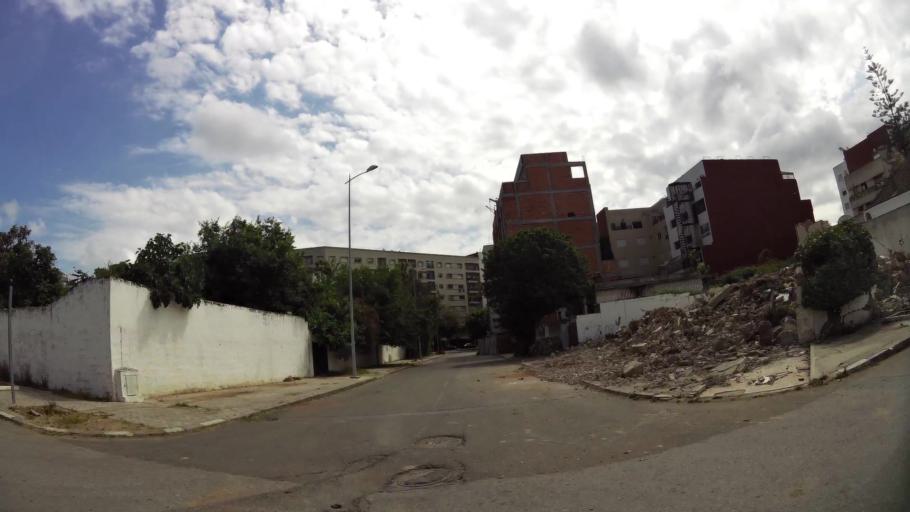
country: MA
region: Gharb-Chrarda-Beni Hssen
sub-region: Kenitra Province
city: Kenitra
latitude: 34.2558
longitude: -6.5776
